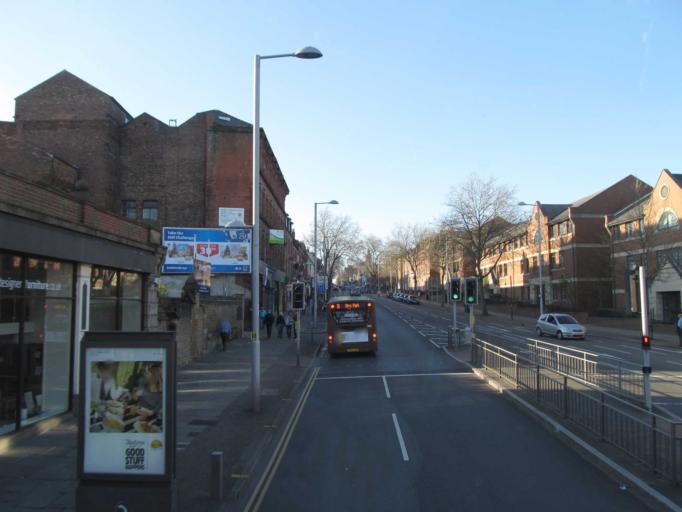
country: GB
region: England
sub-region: Nottingham
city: Nottingham
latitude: 52.9596
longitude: -1.1496
